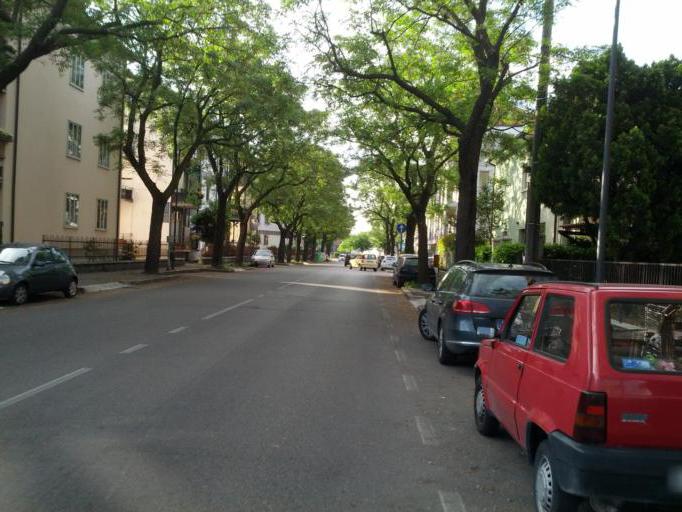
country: IT
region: Veneto
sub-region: Provincia di Verona
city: Montorio
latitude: 45.4357
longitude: 11.0457
